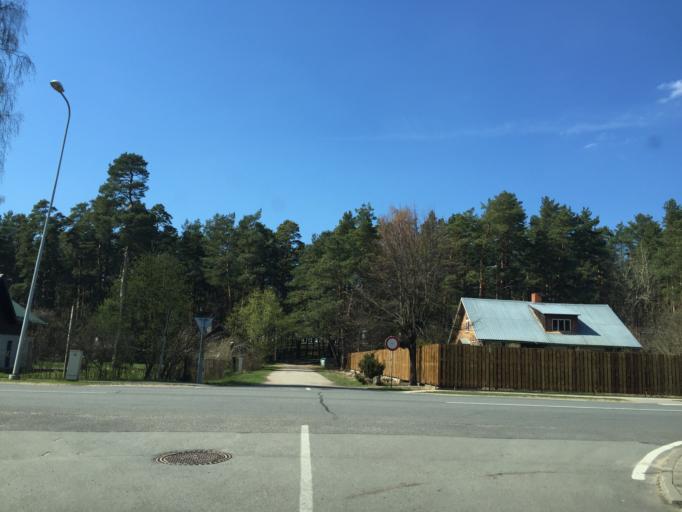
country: LV
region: Saulkrastu
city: Saulkrasti
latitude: 57.2435
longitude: 24.4025
